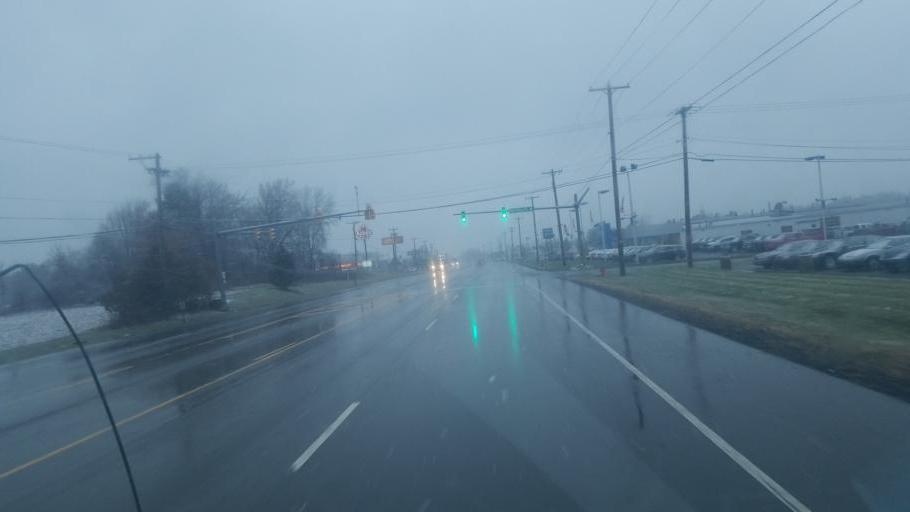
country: US
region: Ohio
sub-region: Richland County
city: Shelby
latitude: 40.8638
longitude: -82.6390
